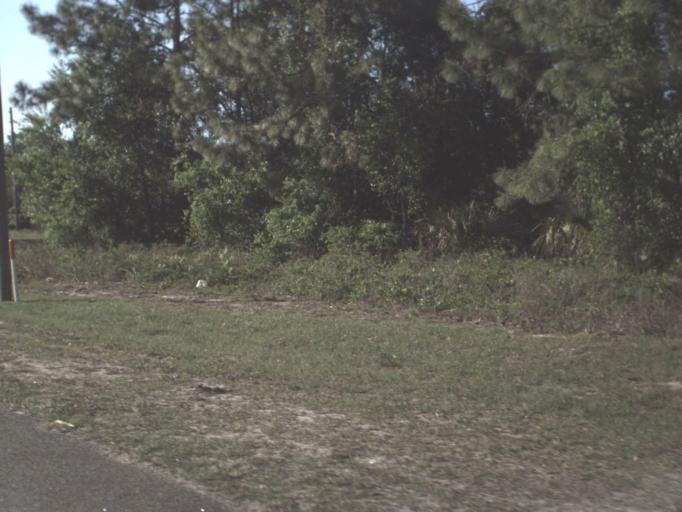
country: US
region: Florida
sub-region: Lake County
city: Mount Plymouth
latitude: 28.8126
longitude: -81.4666
